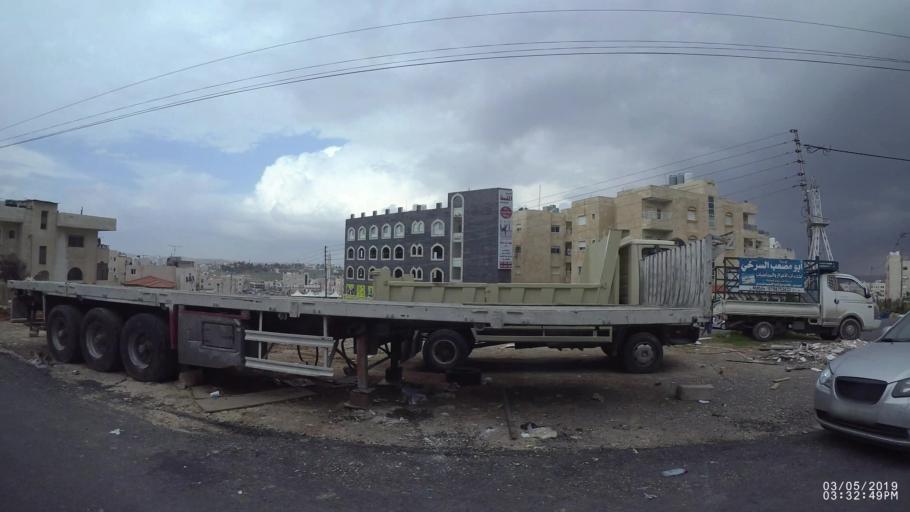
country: JO
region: Amman
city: Amman
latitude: 32.0048
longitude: 35.9500
